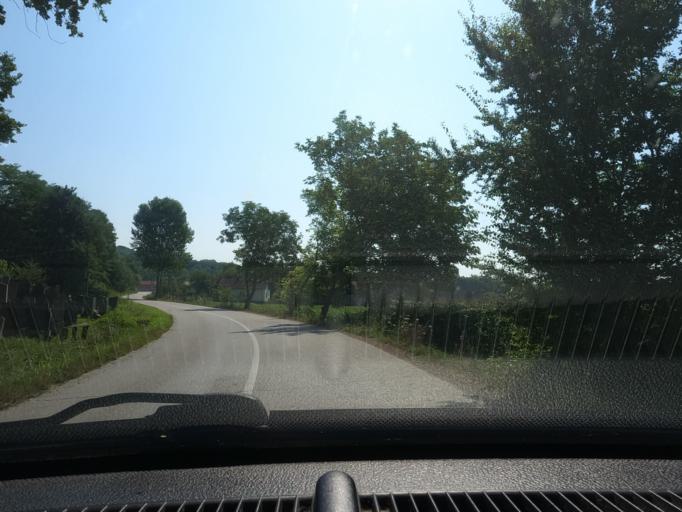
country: RS
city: Jadranska Lesnica
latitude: 44.5503
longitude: 19.3346
